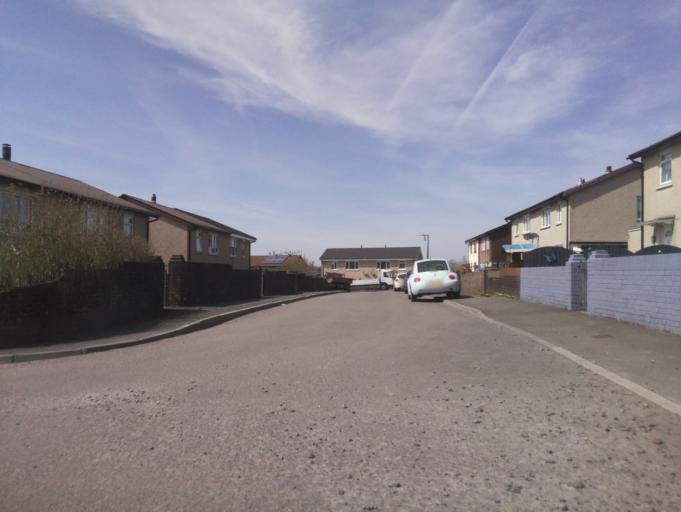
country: GB
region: Wales
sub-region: Merthyr Tydfil County Borough
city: Merthyr Tydfil
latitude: 51.7734
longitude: -3.3501
